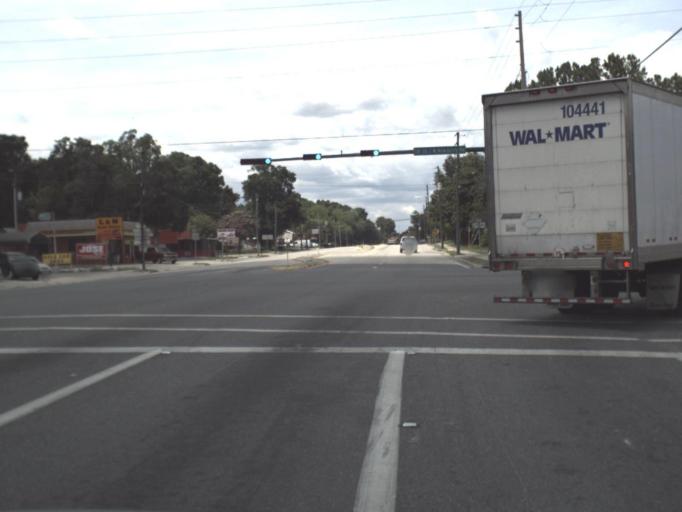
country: US
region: Florida
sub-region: Alachua County
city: Newberry
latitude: 29.6463
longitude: -82.6065
